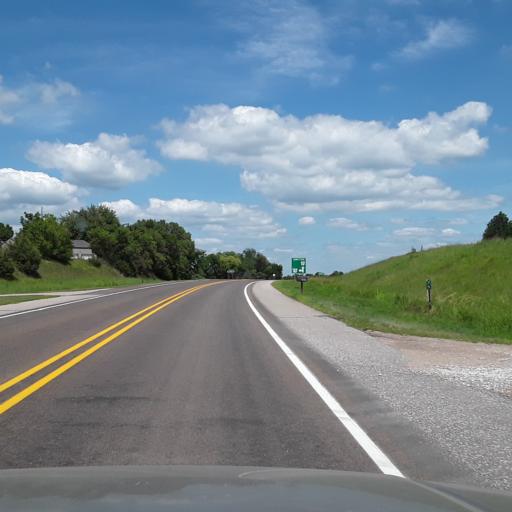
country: US
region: Nebraska
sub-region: Nance County
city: Genoa
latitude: 41.4654
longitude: -97.7217
